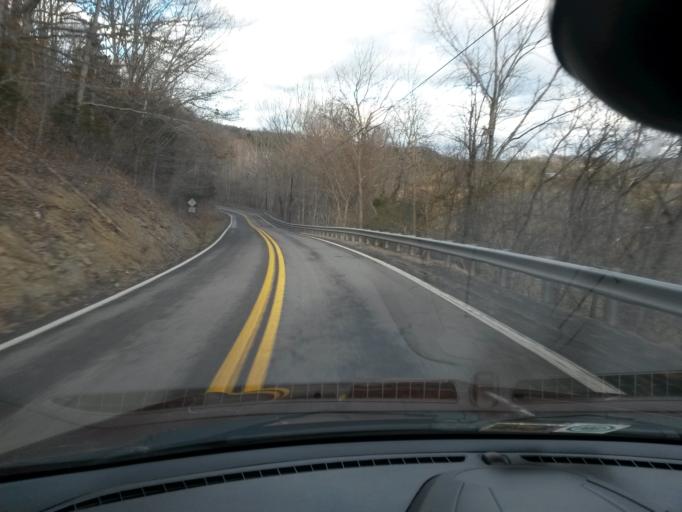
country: US
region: West Virginia
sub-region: Monroe County
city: Union
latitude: 37.5435
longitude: -80.5927
